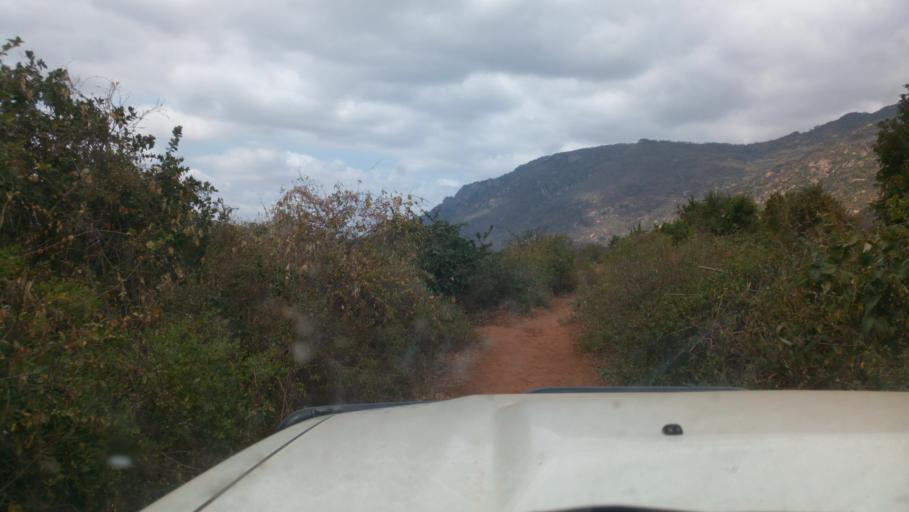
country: KE
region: Kitui
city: Kitui
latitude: -1.8702
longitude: 38.3643
